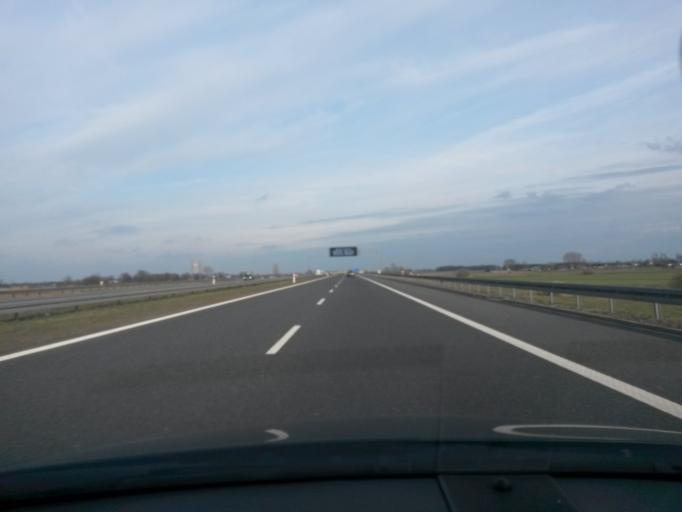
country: PL
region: Lodz Voivodeship
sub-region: Powiat poddebicki
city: Wartkowice
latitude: 51.9982
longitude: 19.0156
